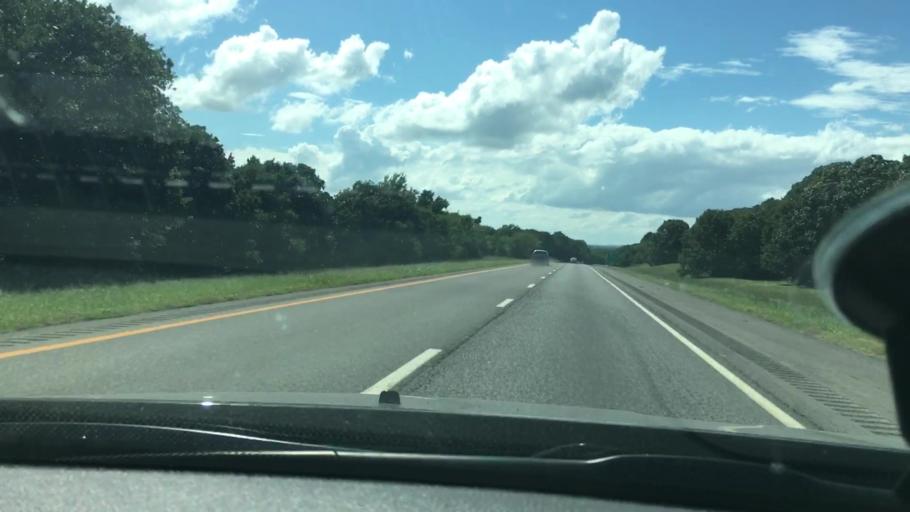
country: US
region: Oklahoma
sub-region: Sequoyah County
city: Vian
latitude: 35.4908
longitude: -95.0659
